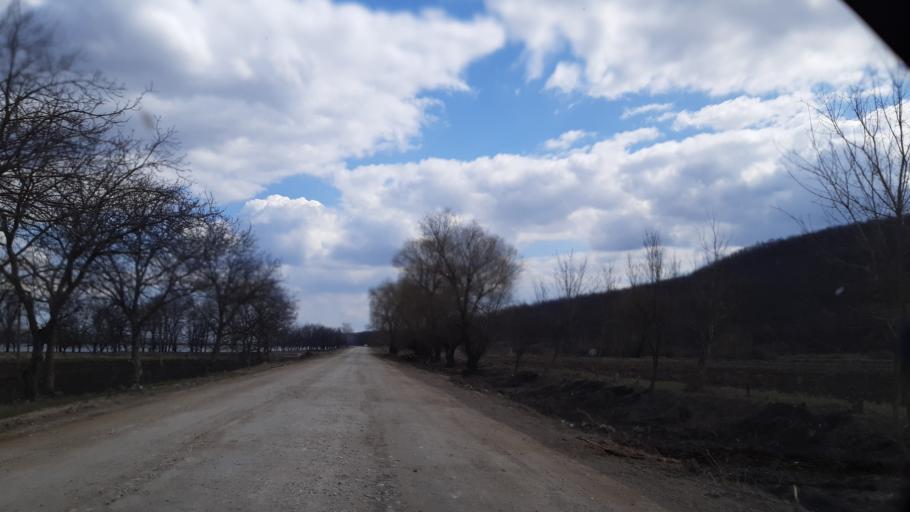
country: MD
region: Laloveni
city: Ialoveni
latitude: 46.8914
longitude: 28.7284
